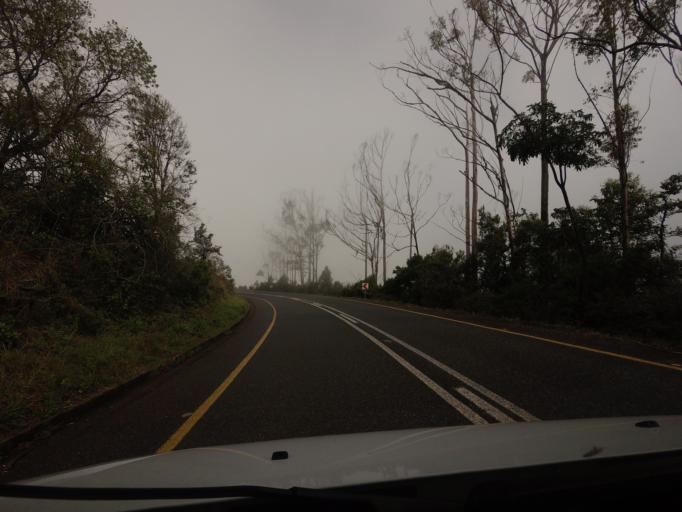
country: ZA
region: Mpumalanga
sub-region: Ehlanzeni District
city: Lydenburg
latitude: -25.1689
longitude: 30.6371
